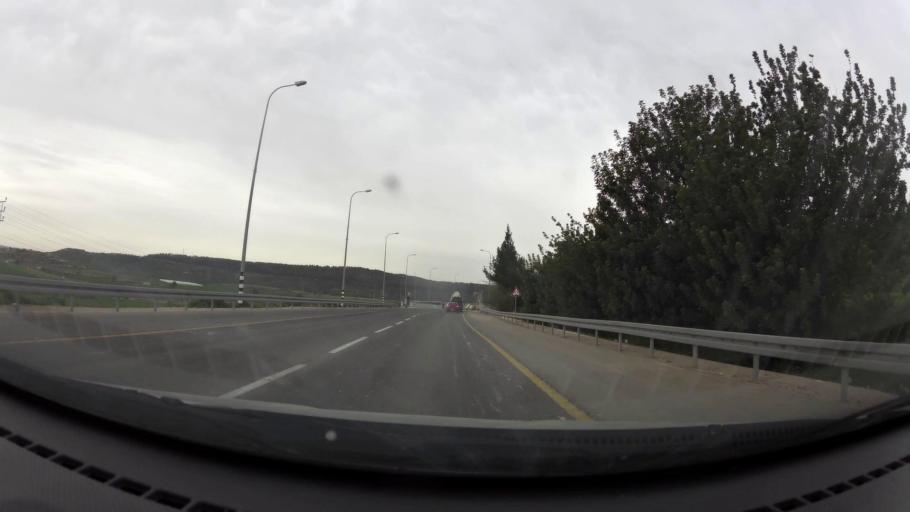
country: IL
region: Jerusalem
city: Bet Shemesh
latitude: 31.6847
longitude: 35.0018
